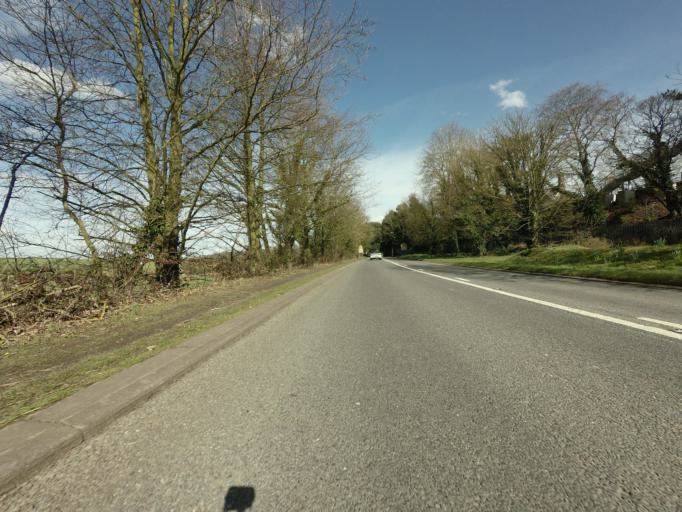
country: GB
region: England
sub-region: Kent
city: Eynsford
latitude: 51.3622
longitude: 0.2034
